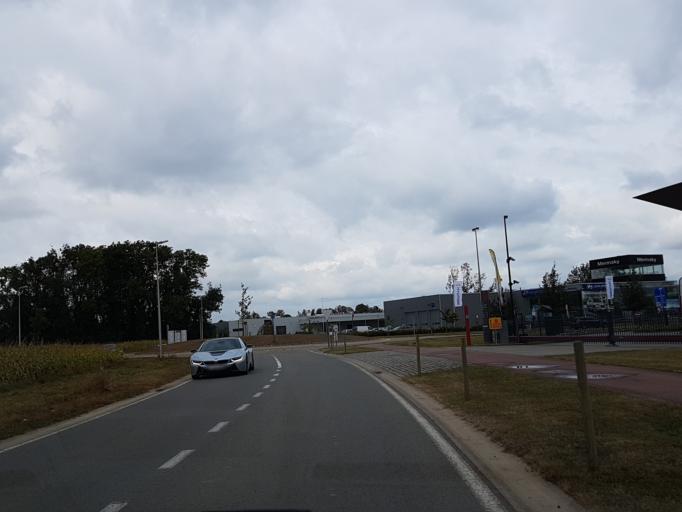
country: BE
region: Flanders
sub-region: Provincie Limburg
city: Sint-Truiden
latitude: 50.8015
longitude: 5.2028
